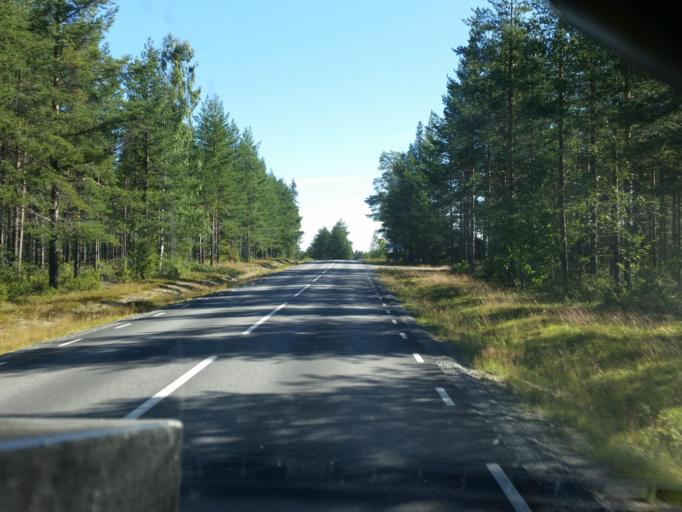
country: SE
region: Vaesterbotten
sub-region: Skelleftea Kommun
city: Storvik
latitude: 65.3359
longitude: 20.8930
